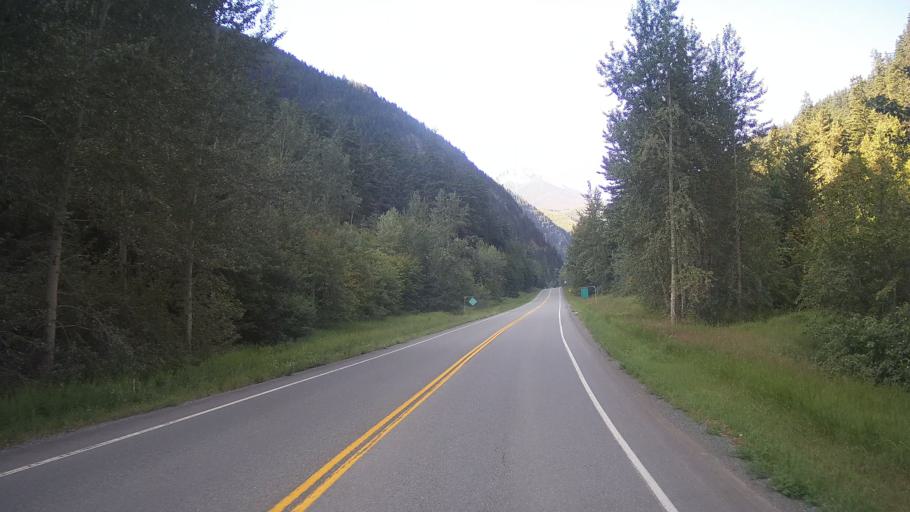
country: CA
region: British Columbia
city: Lillooet
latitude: 50.5611
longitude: -122.0916
